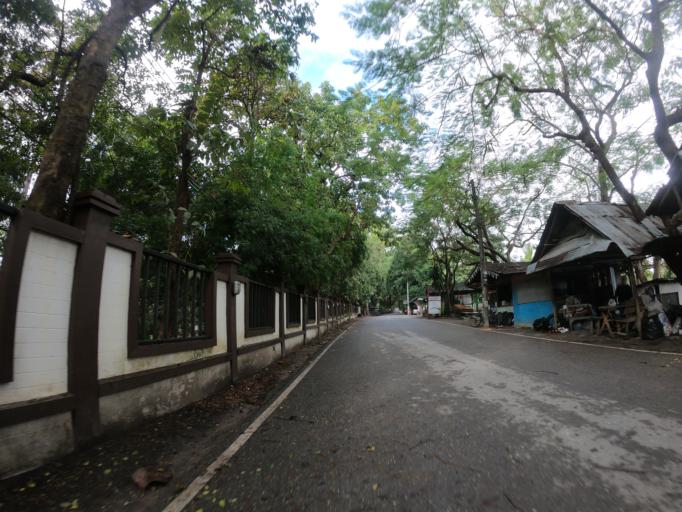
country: TH
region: Chiang Mai
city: Chiang Mai
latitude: 18.8200
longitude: 98.9750
